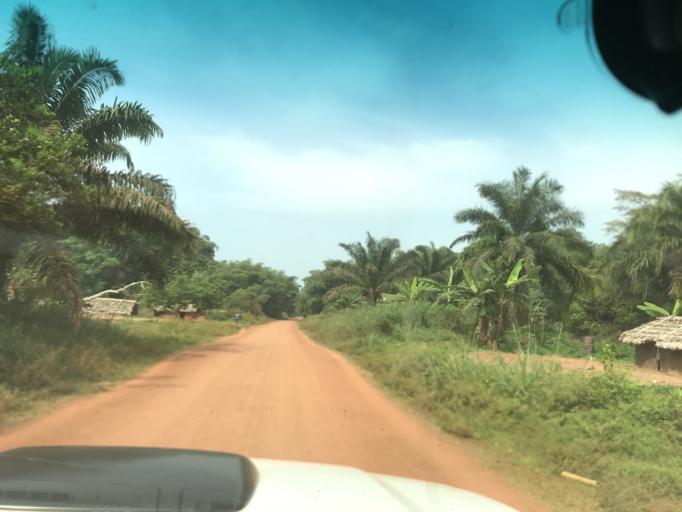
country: CD
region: Eastern Province
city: Buta
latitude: 2.8542
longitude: 24.5290
